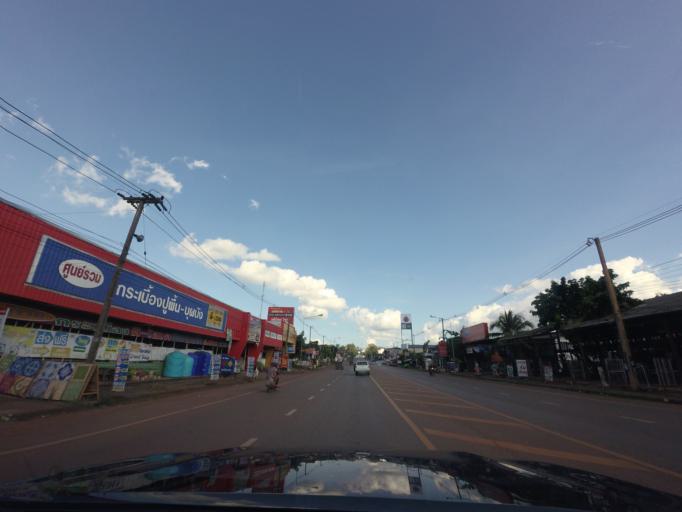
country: TH
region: Changwat Udon Thani
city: Ban Dung
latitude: 17.7038
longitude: 103.2542
